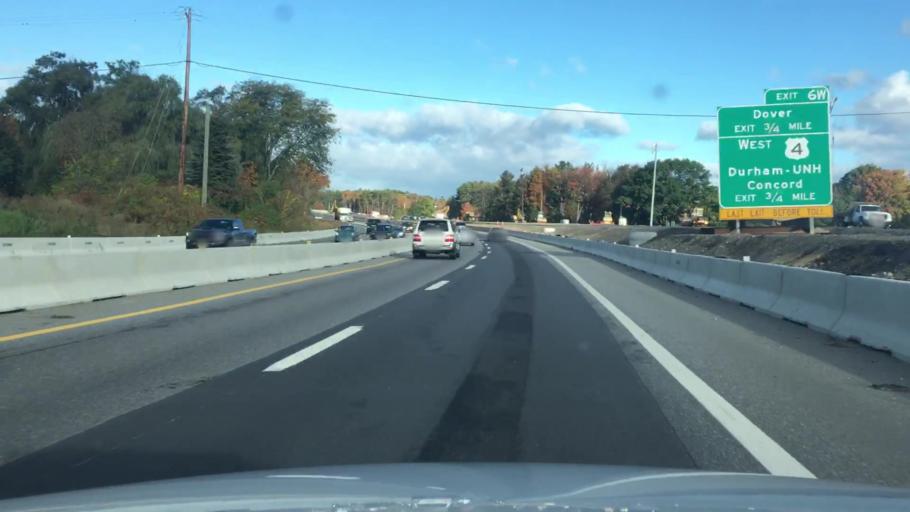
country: US
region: Maine
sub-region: York County
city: Eliot
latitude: 43.1225
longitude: -70.8307
